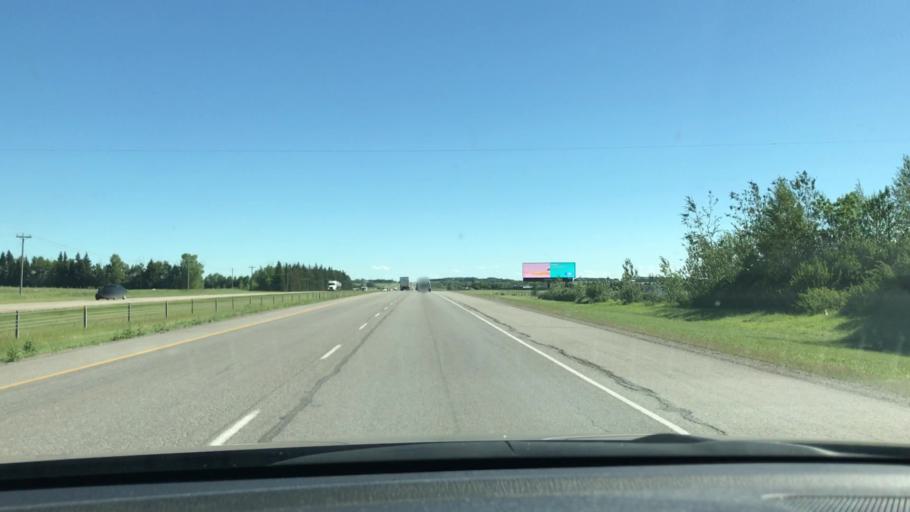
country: CA
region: Alberta
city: Olds
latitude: 51.9215
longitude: -114.0255
